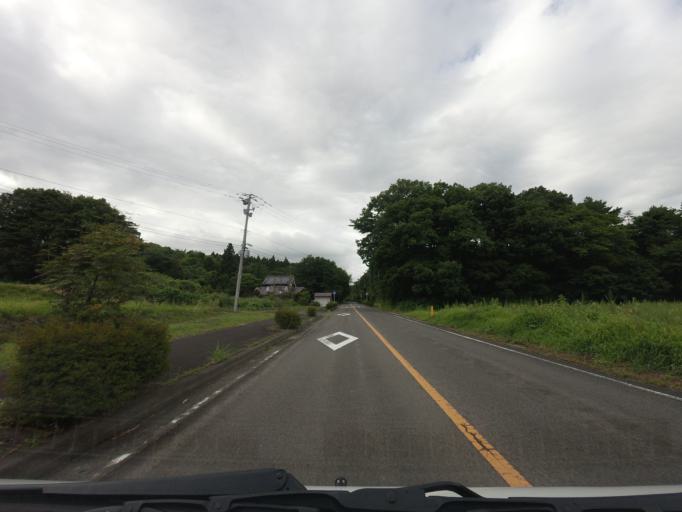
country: JP
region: Fukushima
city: Motomiya
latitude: 37.5731
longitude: 140.3489
